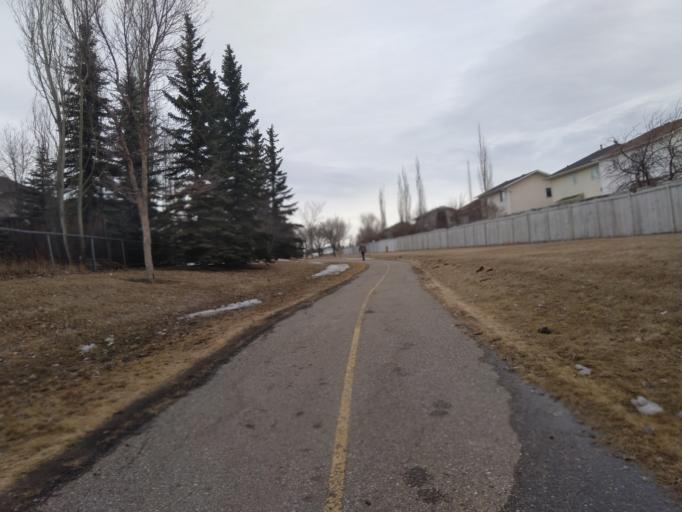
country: CA
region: Alberta
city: Calgary
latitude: 51.1552
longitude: -114.0481
